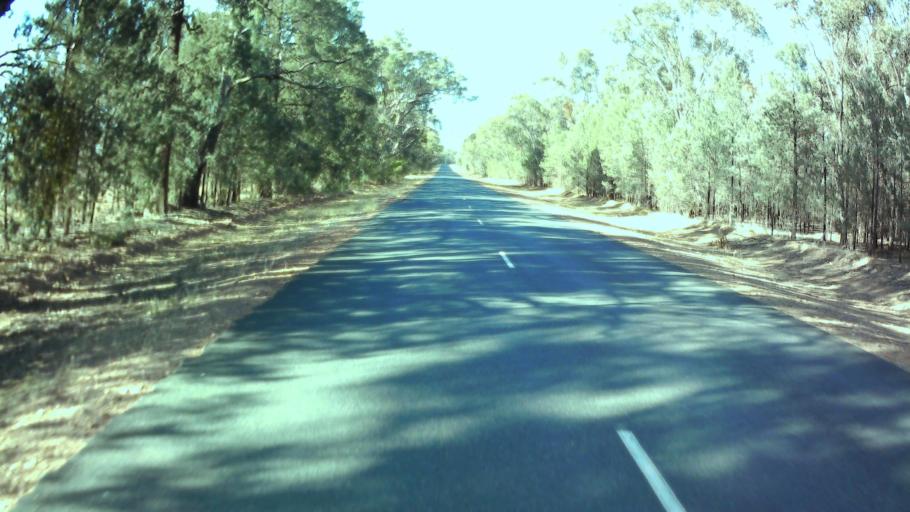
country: AU
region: New South Wales
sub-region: Weddin
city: Grenfell
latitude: -34.0232
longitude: 148.0992
